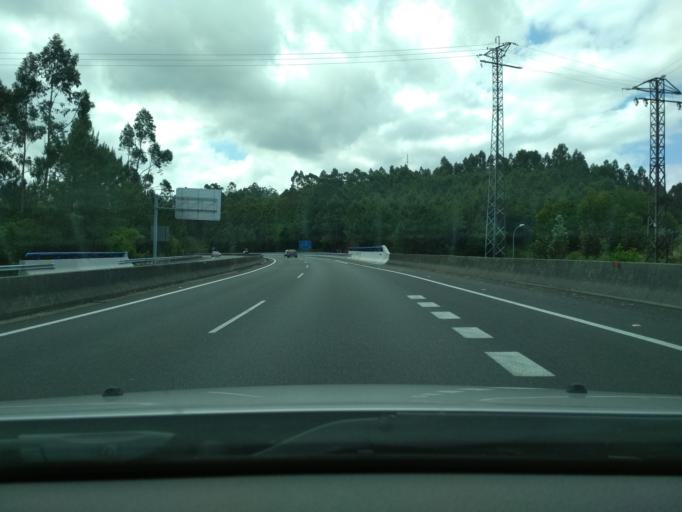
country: ES
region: Galicia
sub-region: Provincia de Pontevedra
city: Portas
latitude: 42.5950
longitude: -8.6778
